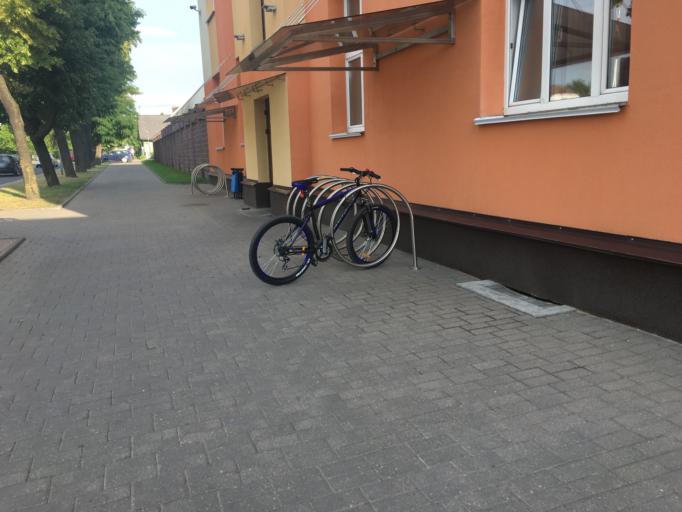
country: BY
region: Grodnenskaya
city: Hrodna
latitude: 53.6671
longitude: 23.8219
